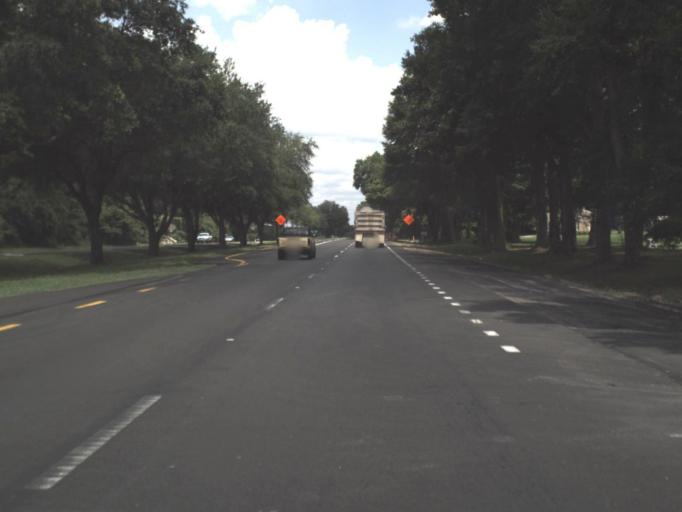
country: US
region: Florida
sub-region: Alachua County
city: Alachua
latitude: 29.7734
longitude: -82.4372
